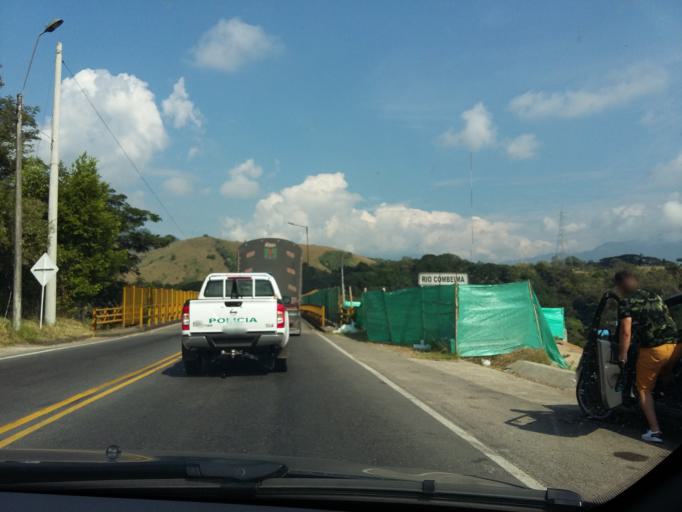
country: CO
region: Tolima
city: Ibague
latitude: 4.4047
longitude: -75.1803
